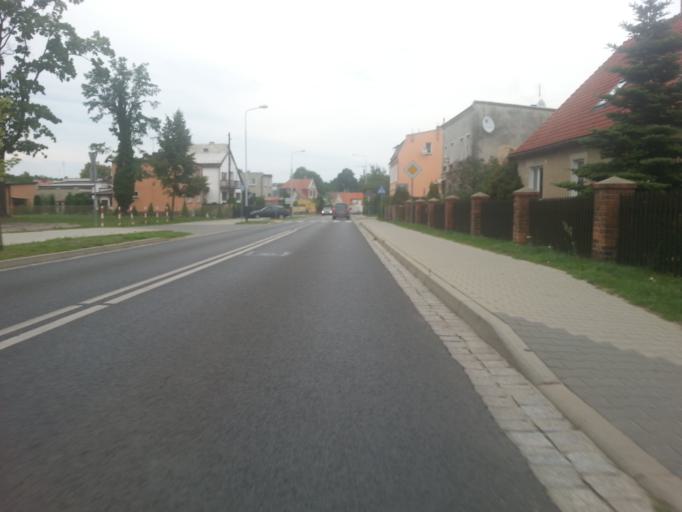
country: PL
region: Lower Silesian Voivodeship
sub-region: Powiat olesnicki
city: Twardogora
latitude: 51.3655
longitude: 17.4598
